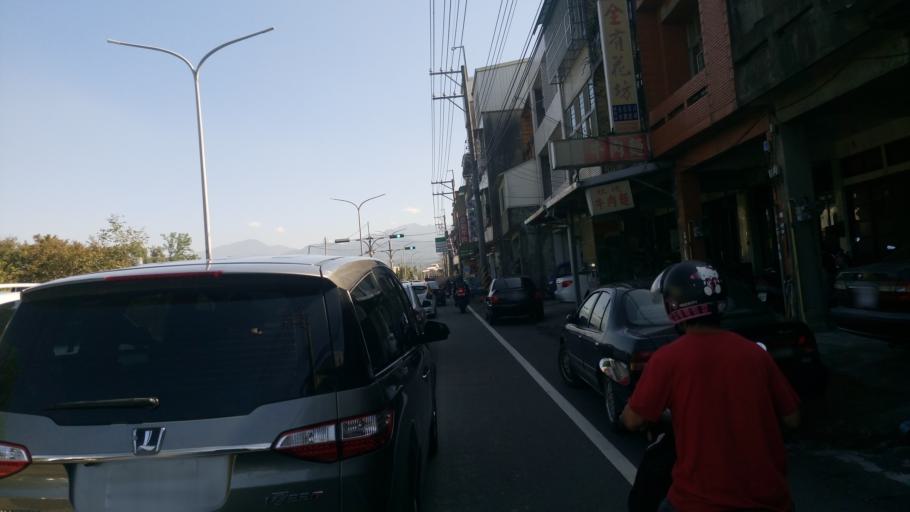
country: TW
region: Taiwan
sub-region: Hsinchu
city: Zhubei
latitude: 24.7205
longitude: 121.1155
